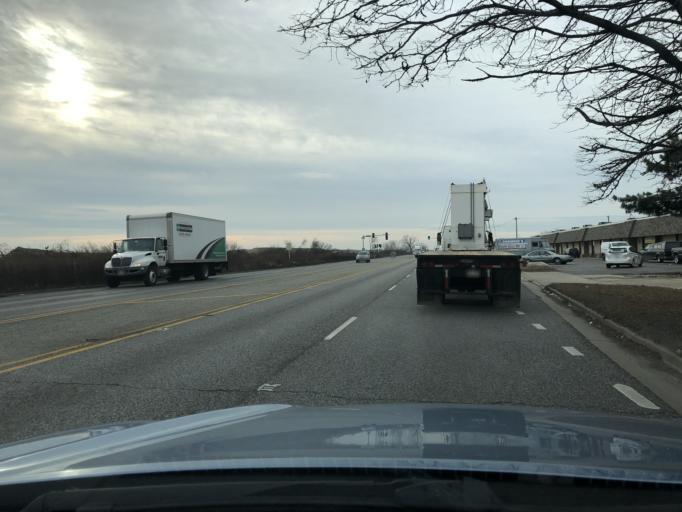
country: US
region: Illinois
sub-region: Cook County
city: Elk Grove Village
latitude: 41.9952
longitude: -87.9401
